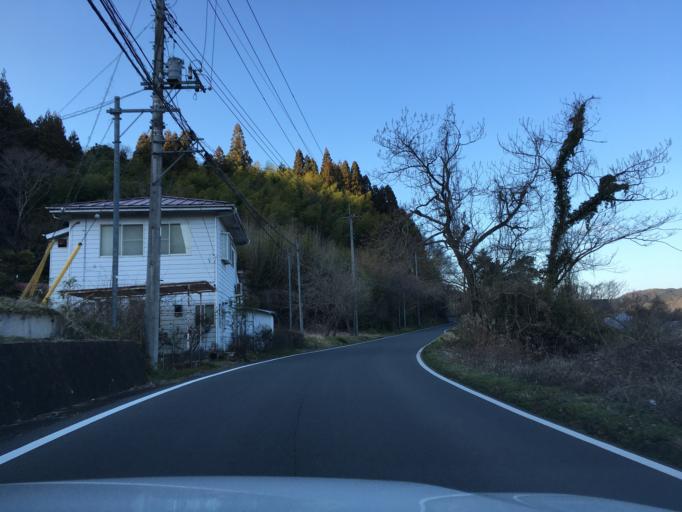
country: JP
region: Tochigi
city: Karasuyama
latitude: 36.7716
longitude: 140.2058
